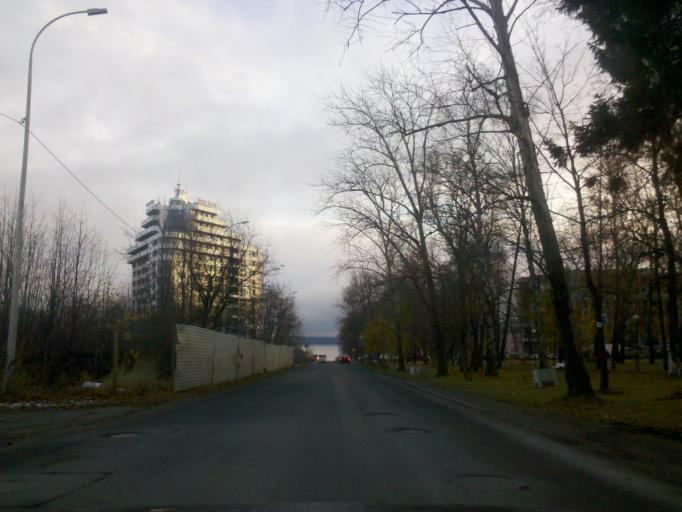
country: RU
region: Republic of Karelia
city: Petrozavodsk
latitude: 61.7941
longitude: 34.3692
